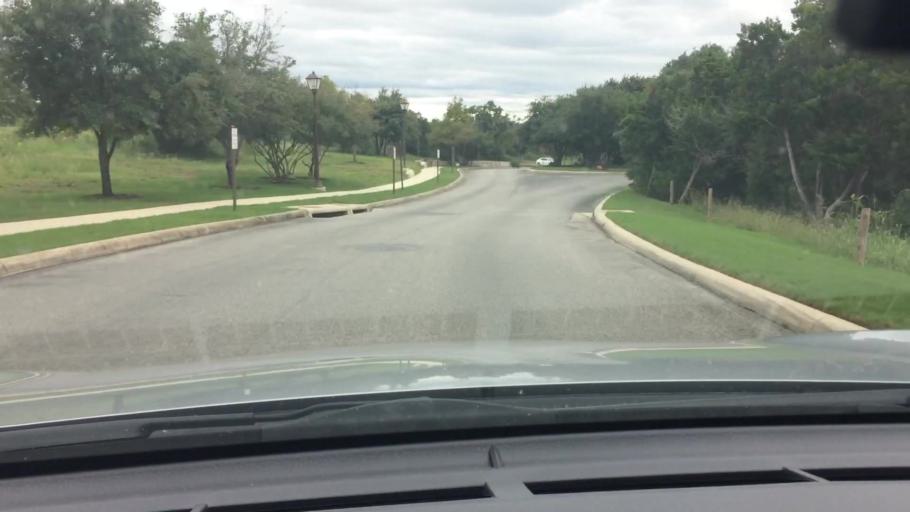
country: US
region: Texas
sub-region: Bexar County
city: Timberwood Park
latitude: 29.6634
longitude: -98.4003
